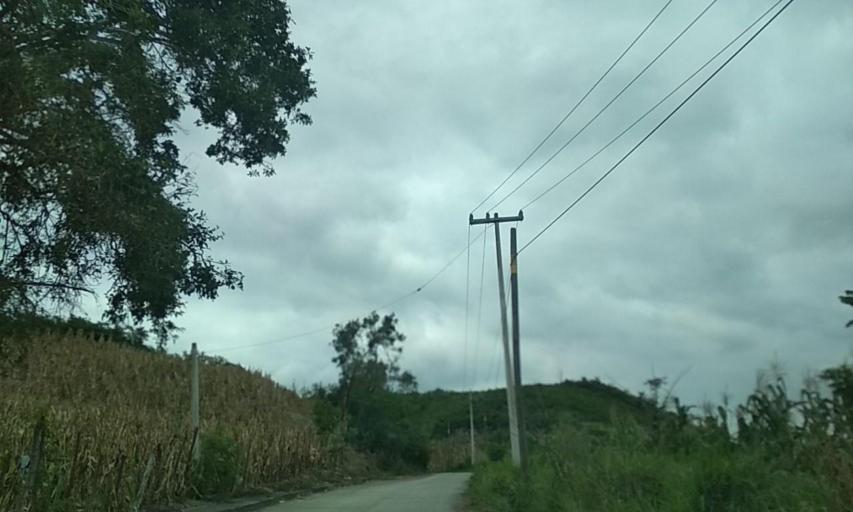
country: MX
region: Veracruz
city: Papantla de Olarte
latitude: 20.4701
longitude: -97.3210
